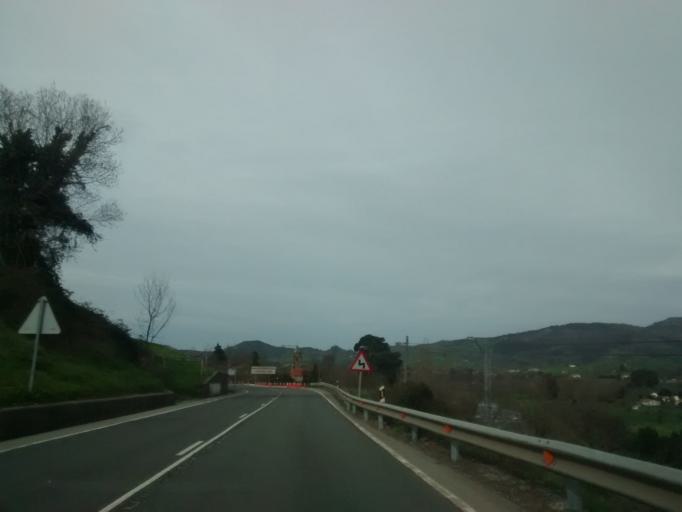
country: ES
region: Cantabria
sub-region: Provincia de Cantabria
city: Santiurde de Toranzo
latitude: 43.2431
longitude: -3.9471
